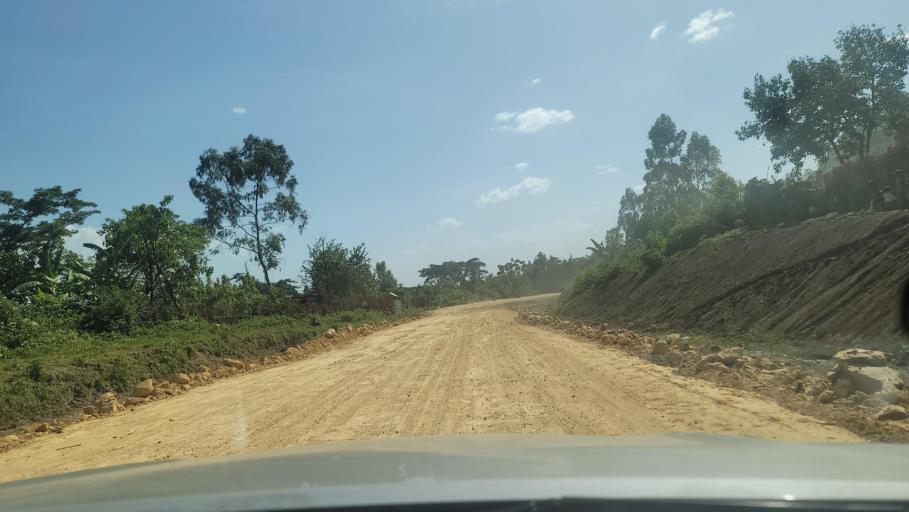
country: ET
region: Oromiya
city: Agaro
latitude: 7.7958
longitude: 36.3770
